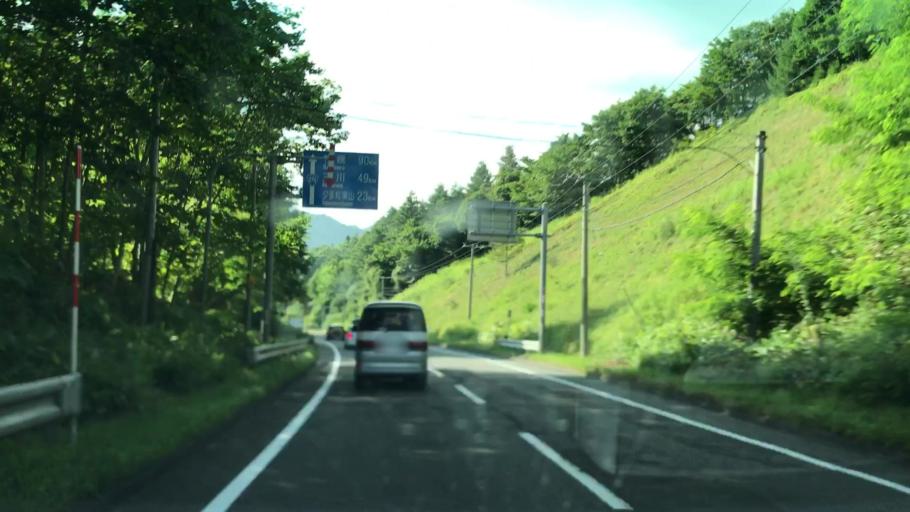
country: JP
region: Hokkaido
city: Shimo-furano
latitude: 42.8883
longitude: 142.2001
